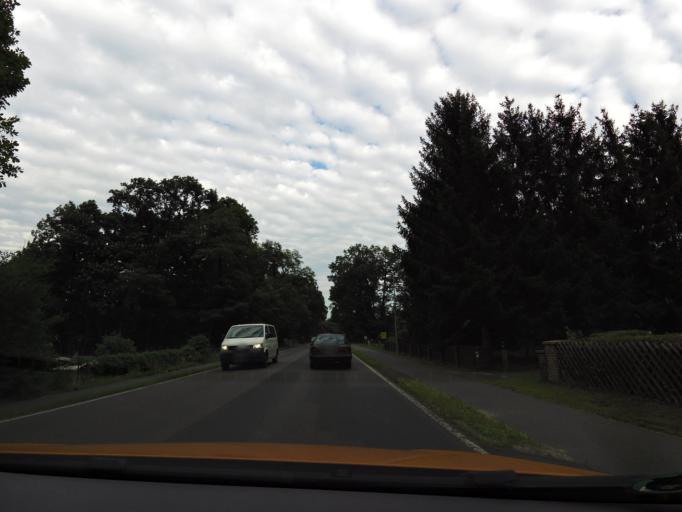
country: DE
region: Brandenburg
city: Roskow
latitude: 52.4092
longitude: 12.7204
